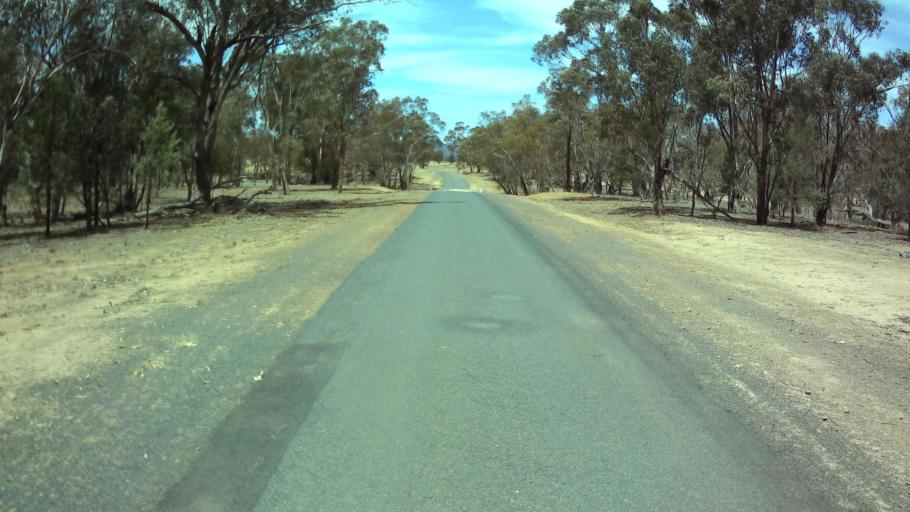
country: AU
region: New South Wales
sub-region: Weddin
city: Grenfell
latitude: -33.7555
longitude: 148.0865
